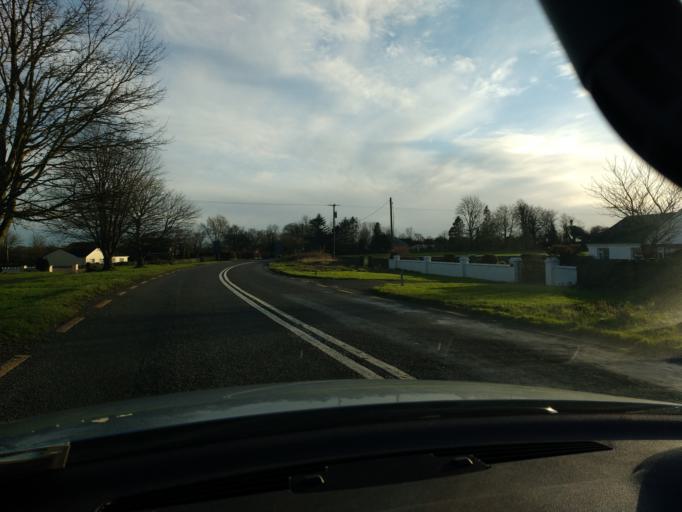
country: IE
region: Munster
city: Thurles
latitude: 52.6567
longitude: -7.7999
